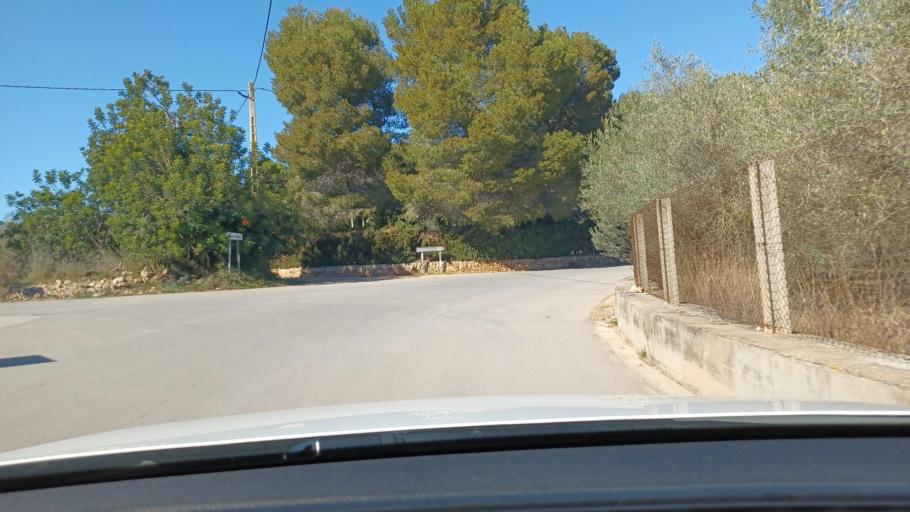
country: ES
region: Catalonia
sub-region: Provincia de Tarragona
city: Masdenverge
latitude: 40.6943
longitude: 0.5412
